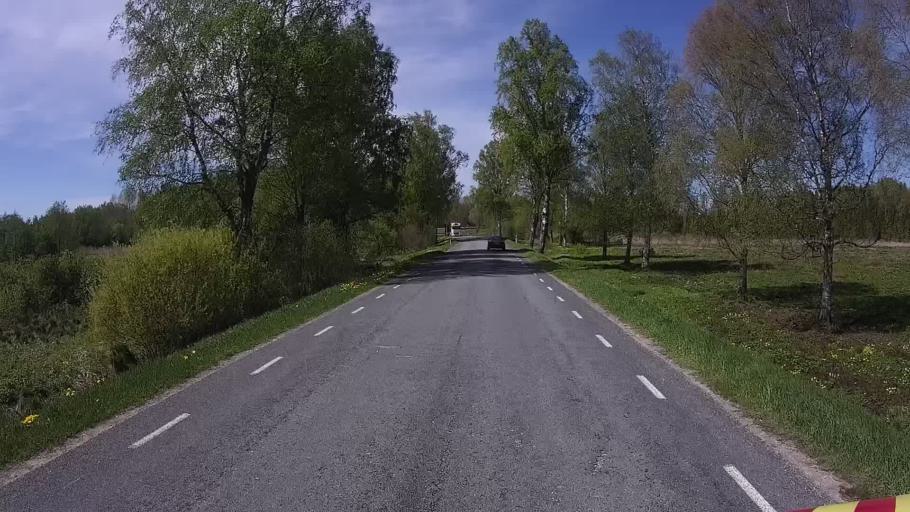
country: LV
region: Apes Novads
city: Ape
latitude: 57.6189
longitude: 26.6039
